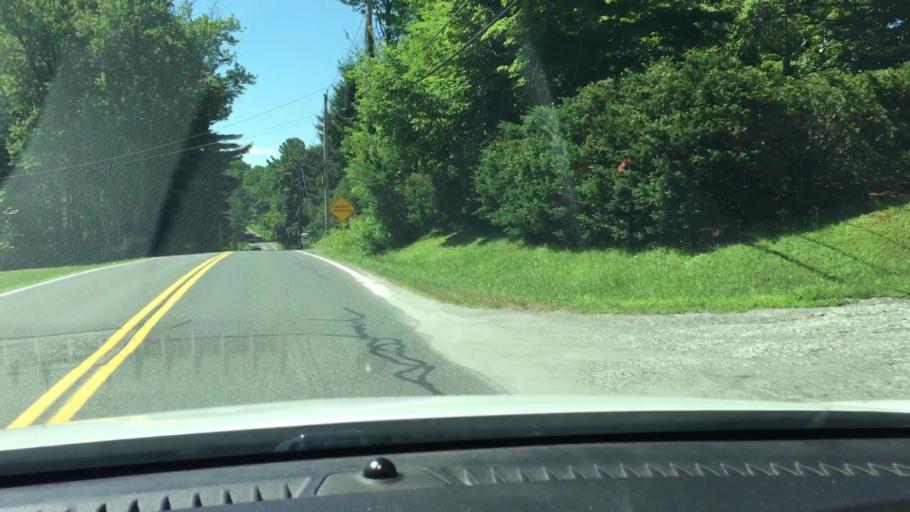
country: US
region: Massachusetts
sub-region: Berkshire County
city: Lenox
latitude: 42.3972
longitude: -73.2549
